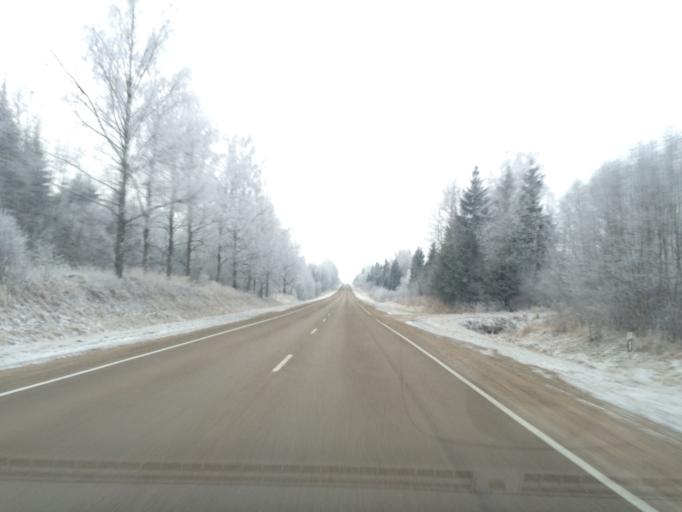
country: LV
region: Rezekne
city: Rezekne
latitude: 56.6256
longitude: 27.4597
